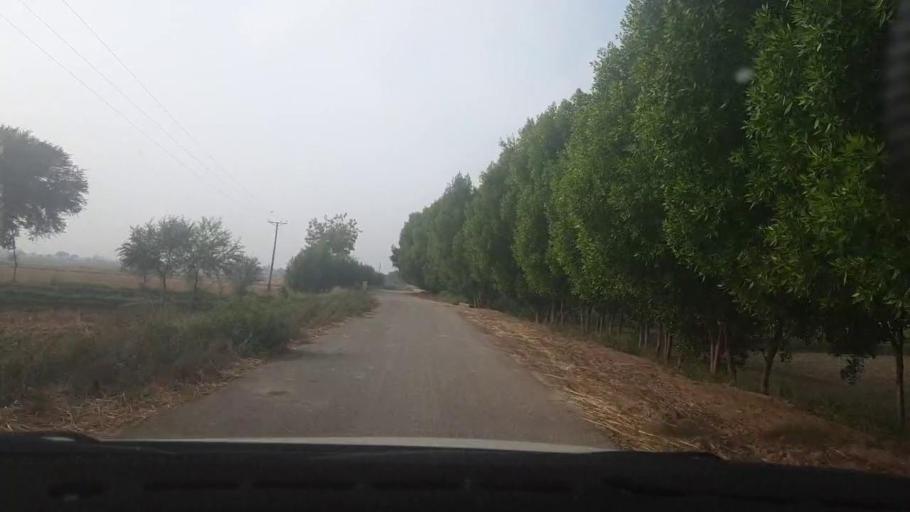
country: PK
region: Sindh
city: Tando Muhammad Khan
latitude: 25.0854
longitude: 68.5153
